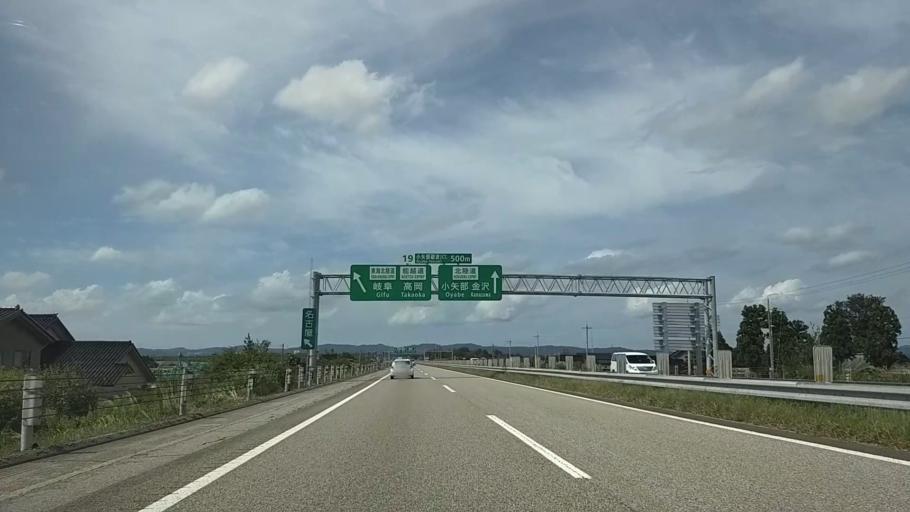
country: JP
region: Toyama
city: Nanto-shi
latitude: 36.6282
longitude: 136.9181
